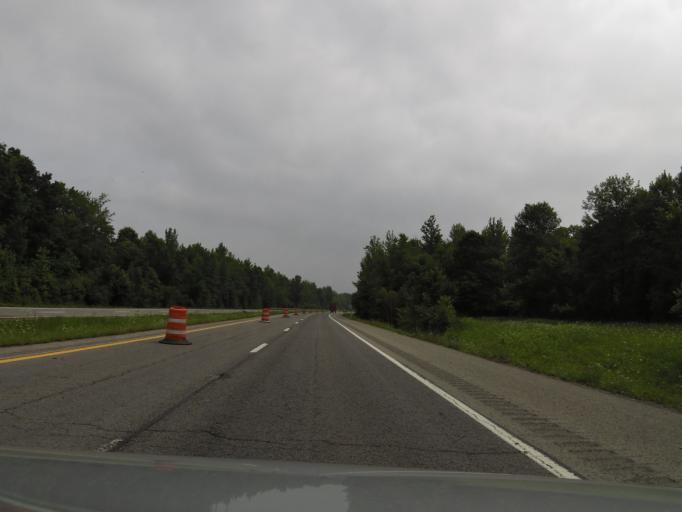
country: US
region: Kentucky
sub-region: Muhlenberg County
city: Morehead
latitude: 37.2685
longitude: -87.1617
